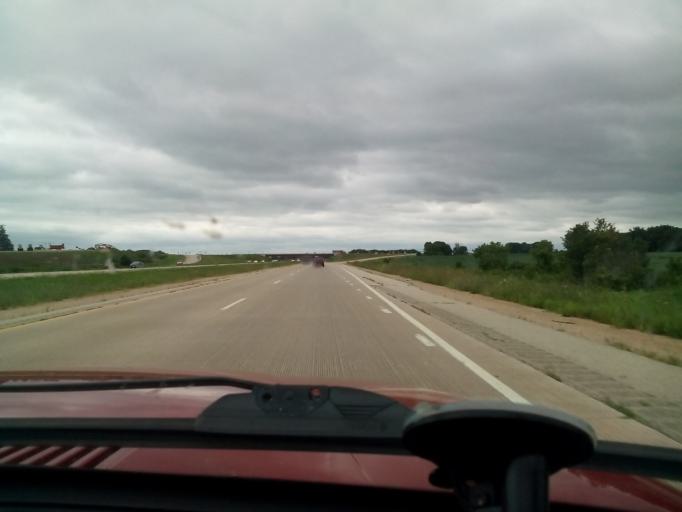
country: US
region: Wisconsin
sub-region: Columbia County
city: Columbus
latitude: 43.3233
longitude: -89.0453
